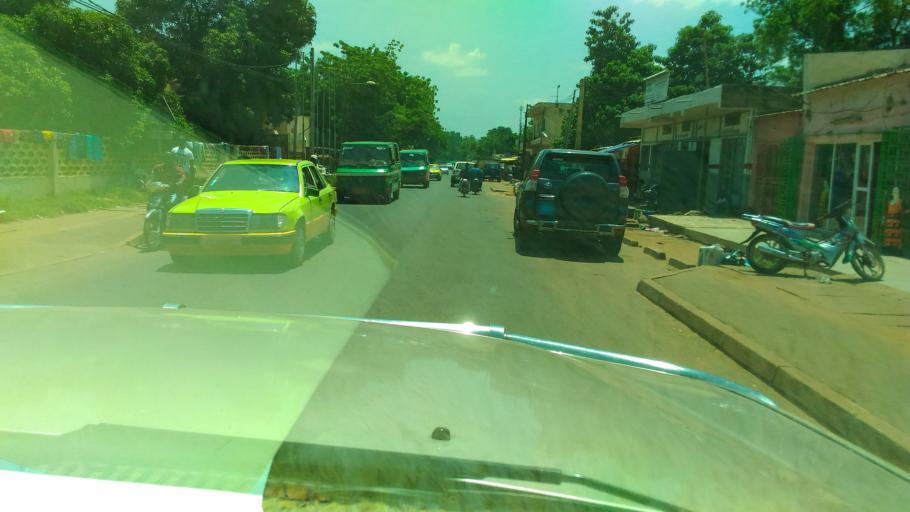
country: ML
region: Bamako
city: Bamako
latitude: 12.6482
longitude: -8.0077
